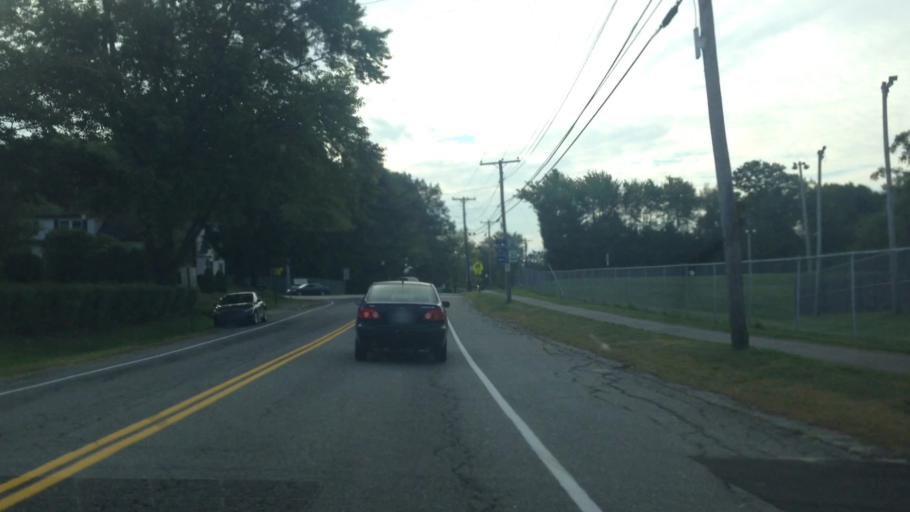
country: US
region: Maine
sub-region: Cumberland County
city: Westbrook
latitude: 43.6727
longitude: -70.3511
